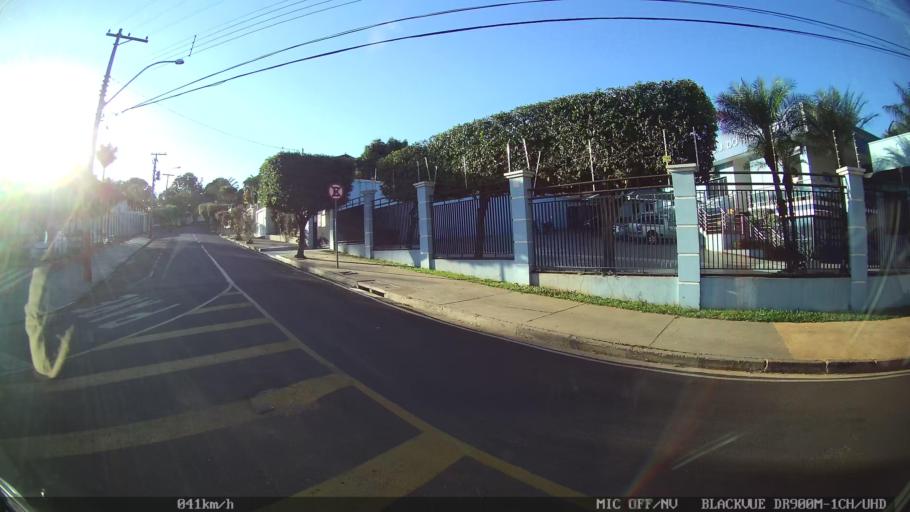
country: BR
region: Sao Paulo
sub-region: Sao Jose Do Rio Preto
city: Sao Jose do Rio Preto
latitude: -20.8084
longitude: -49.3698
